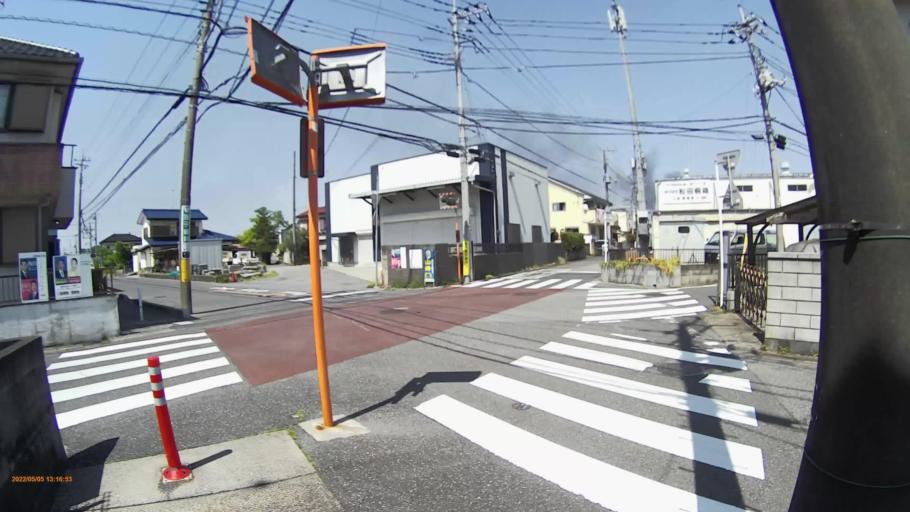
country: JP
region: Saitama
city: Kasukabe
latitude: 35.9695
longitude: 139.7693
